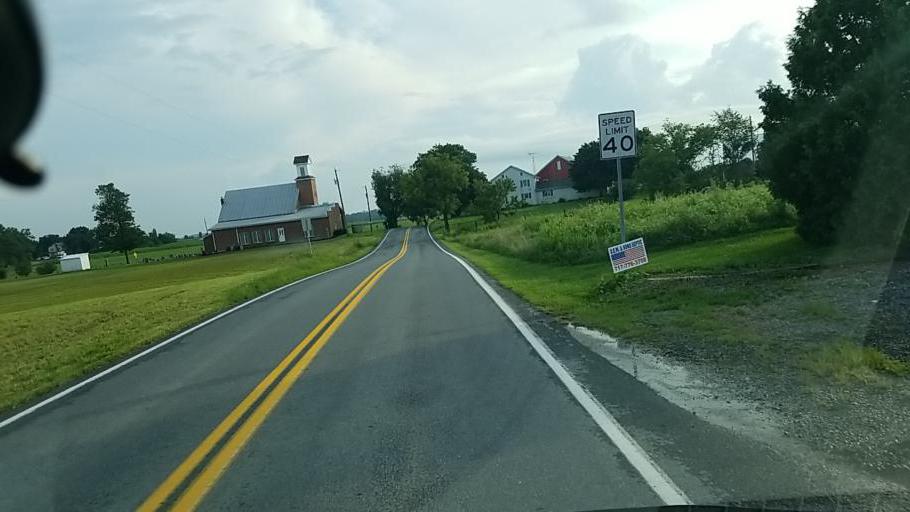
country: US
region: Pennsylvania
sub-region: Cumberland County
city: Newville
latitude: 40.1981
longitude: -77.4806
